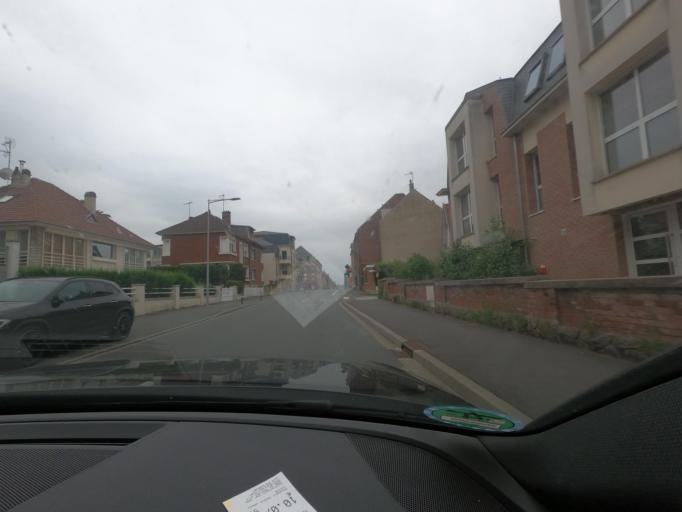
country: FR
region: Picardie
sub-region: Departement de la Somme
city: Amiens
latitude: 49.8781
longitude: 2.3055
